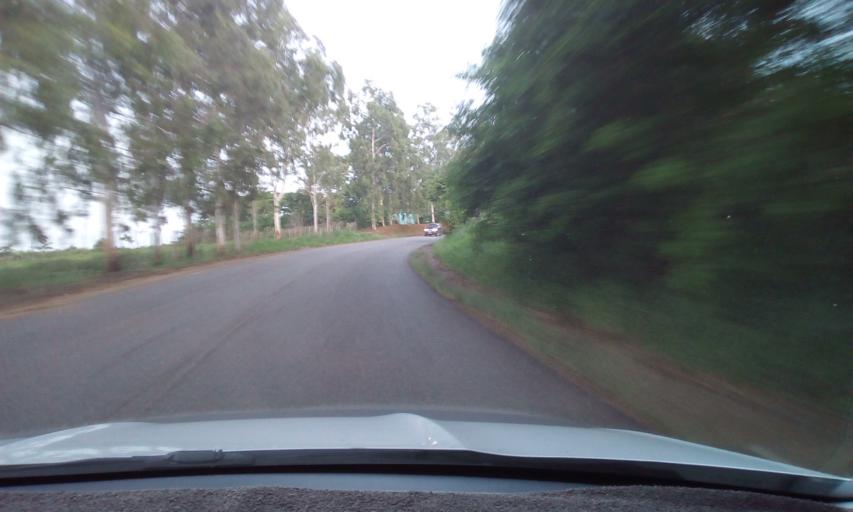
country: BR
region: Pernambuco
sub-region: Condado
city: Condado
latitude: -7.6033
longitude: -35.2107
